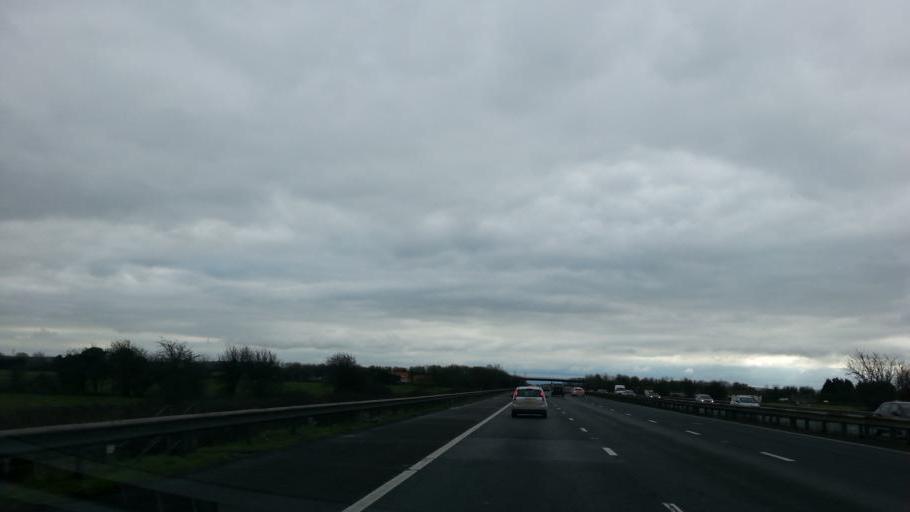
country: GB
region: England
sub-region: Somerset
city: Highbridge
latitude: 51.2018
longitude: -2.9675
